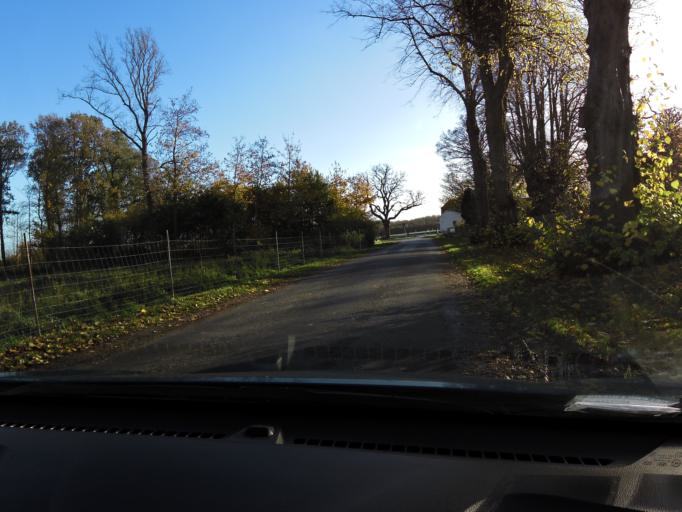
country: DK
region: Central Jutland
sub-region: Odder Kommune
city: Odder
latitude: 55.9152
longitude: 10.2339
